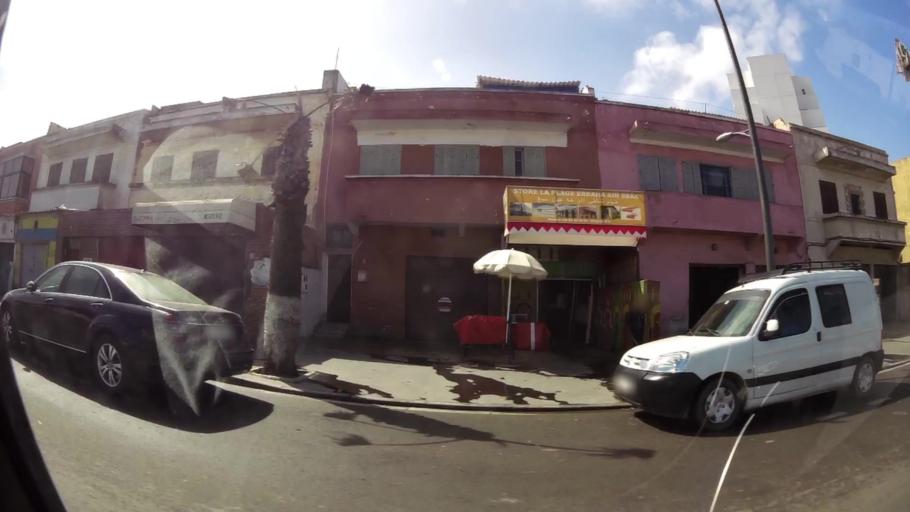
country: MA
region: Grand Casablanca
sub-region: Casablanca
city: Casablanca
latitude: 33.6186
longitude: -7.5427
